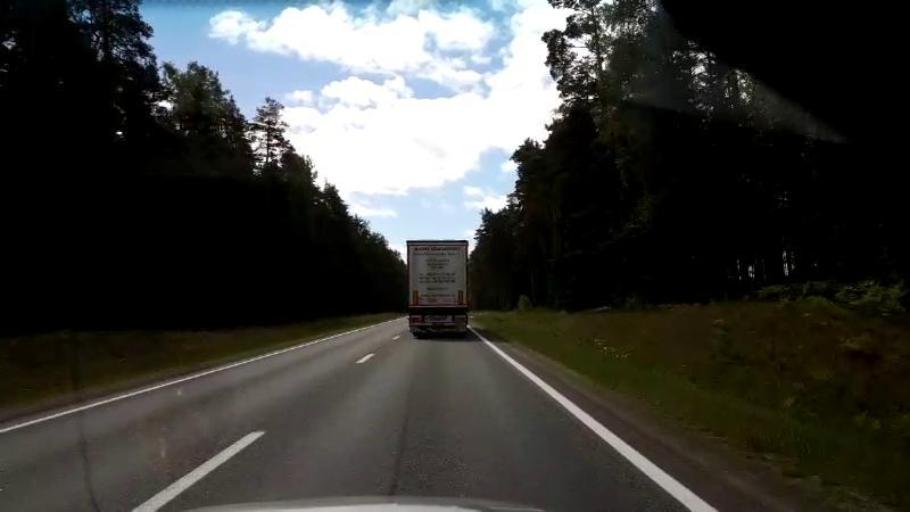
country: LV
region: Salacgrivas
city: Salacgriva
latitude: 57.5629
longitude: 24.4340
